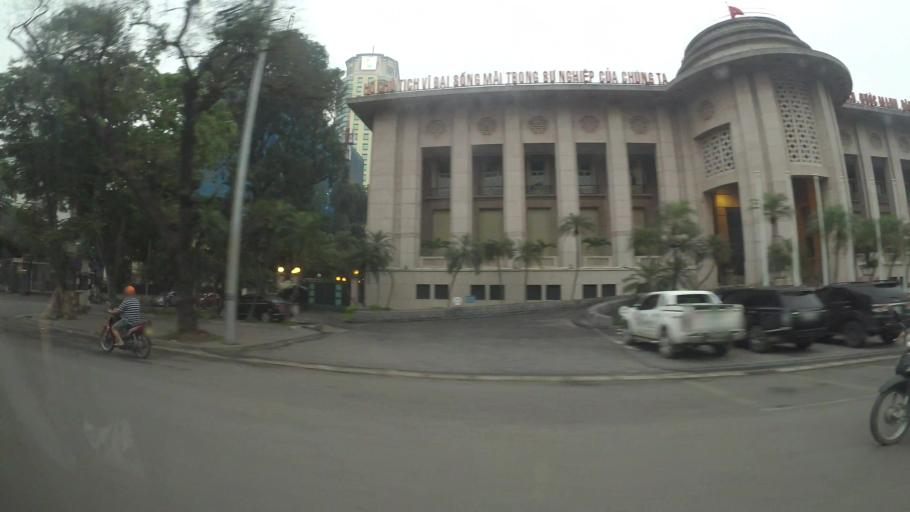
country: VN
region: Ha Noi
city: Hoan Kiem
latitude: 21.0273
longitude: 105.8562
